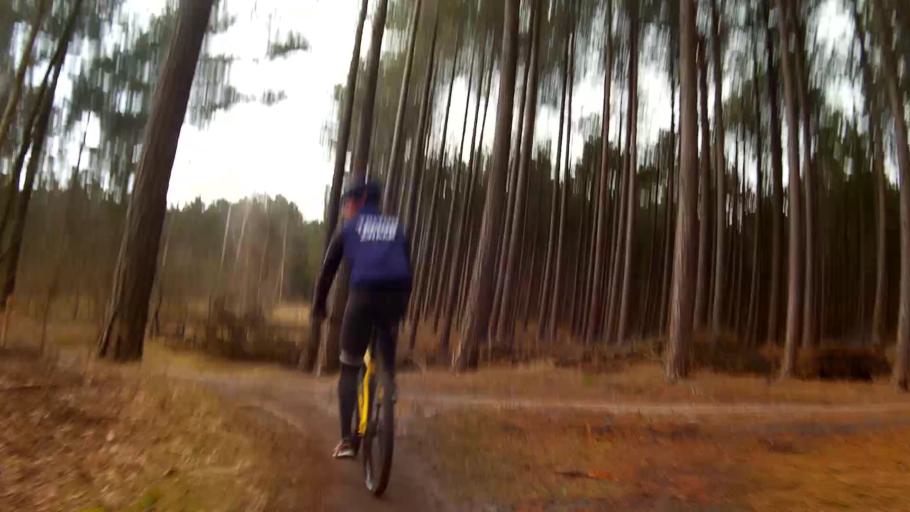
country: NL
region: North Holland
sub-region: Gemeente Bergen
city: Egmond aan Zee
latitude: 52.6876
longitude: 4.6689
